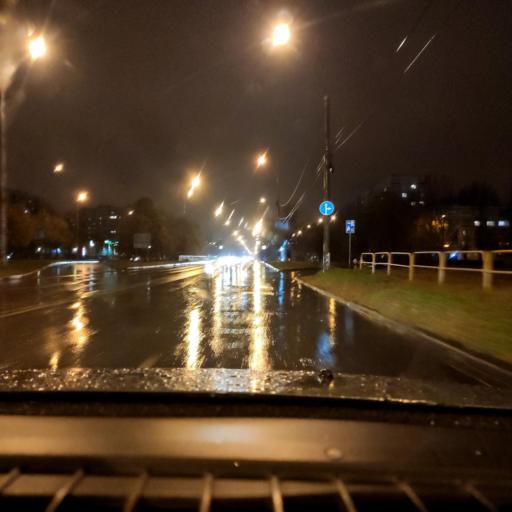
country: RU
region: Samara
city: Tol'yatti
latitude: 53.5346
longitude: 49.3139
